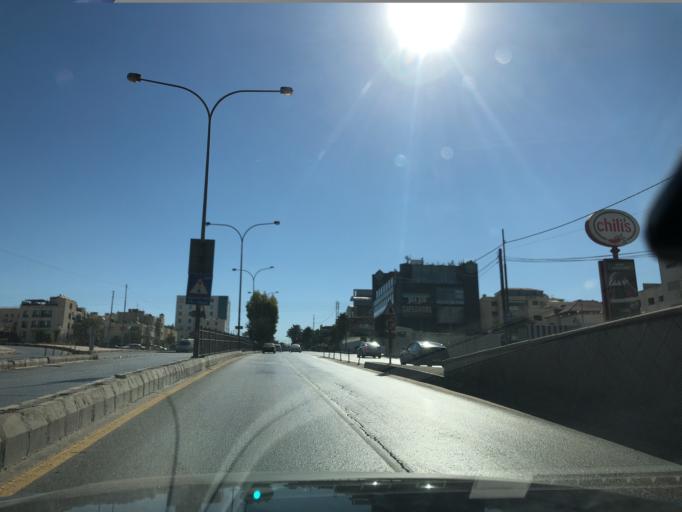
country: JO
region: Amman
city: Al Jubayhah
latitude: 31.9742
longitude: 35.8671
